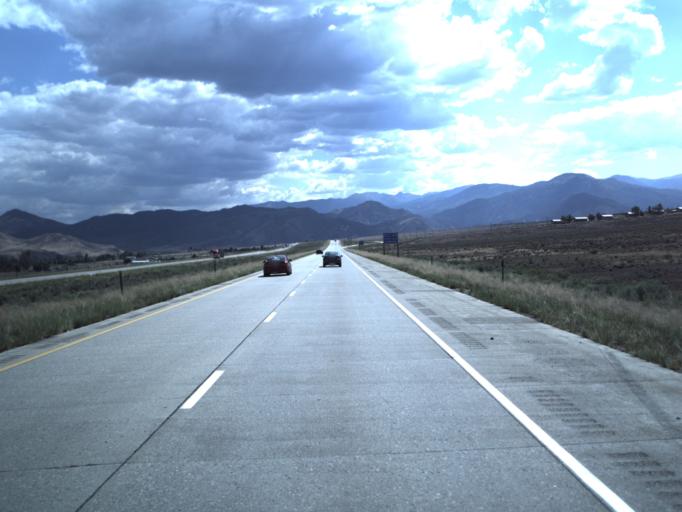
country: US
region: Utah
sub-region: Sevier County
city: Monroe
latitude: 38.6369
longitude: -112.2218
